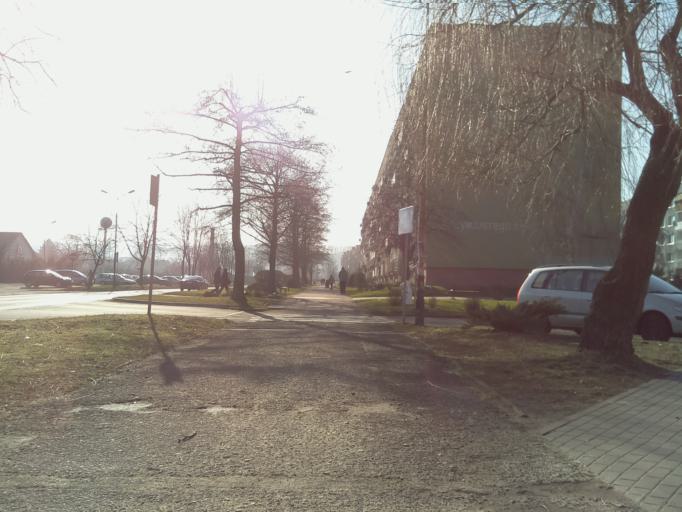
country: PL
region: Lower Silesian Voivodeship
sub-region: Powiat swidnicki
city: Swiebodzice
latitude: 50.8651
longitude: 16.3191
